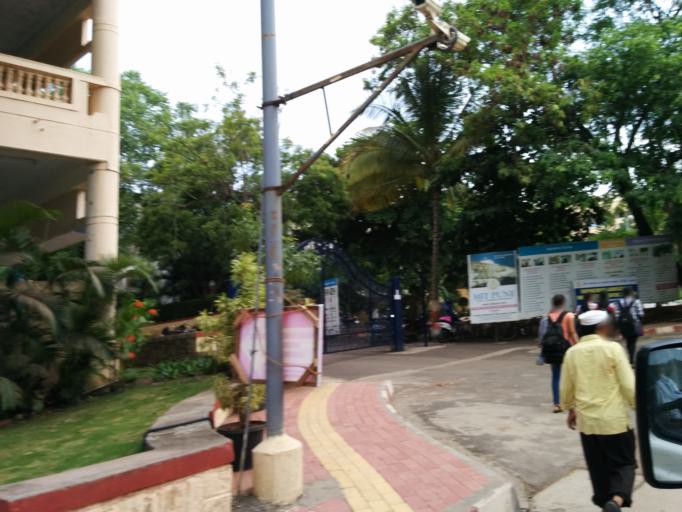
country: IN
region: Maharashtra
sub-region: Pune Division
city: Shivaji Nagar
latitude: 18.5170
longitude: 73.8154
